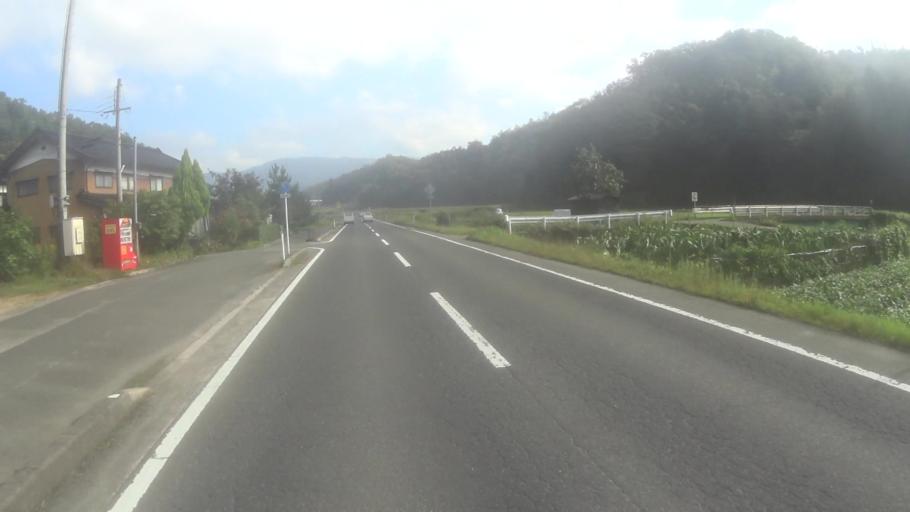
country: JP
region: Kyoto
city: Miyazu
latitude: 35.5823
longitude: 135.1295
